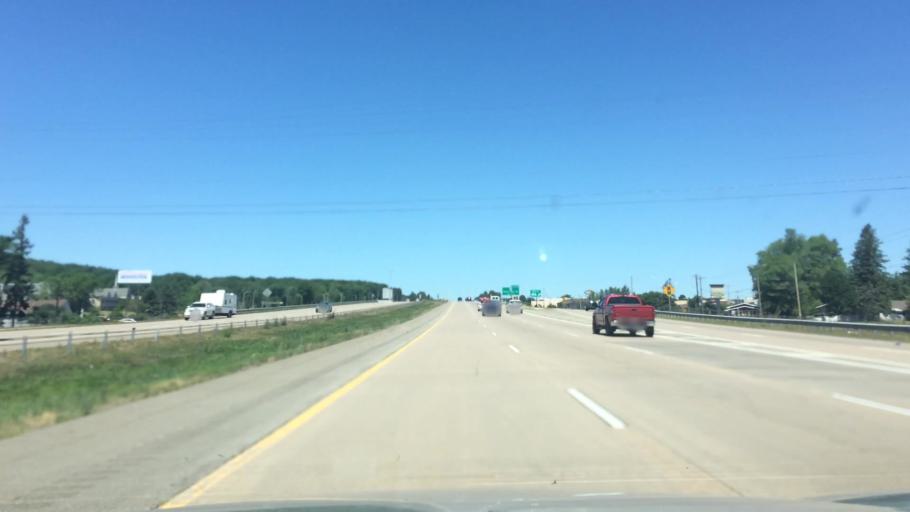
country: US
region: Wisconsin
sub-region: Marathon County
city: Rib Mountain
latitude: 44.9086
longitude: -89.6484
